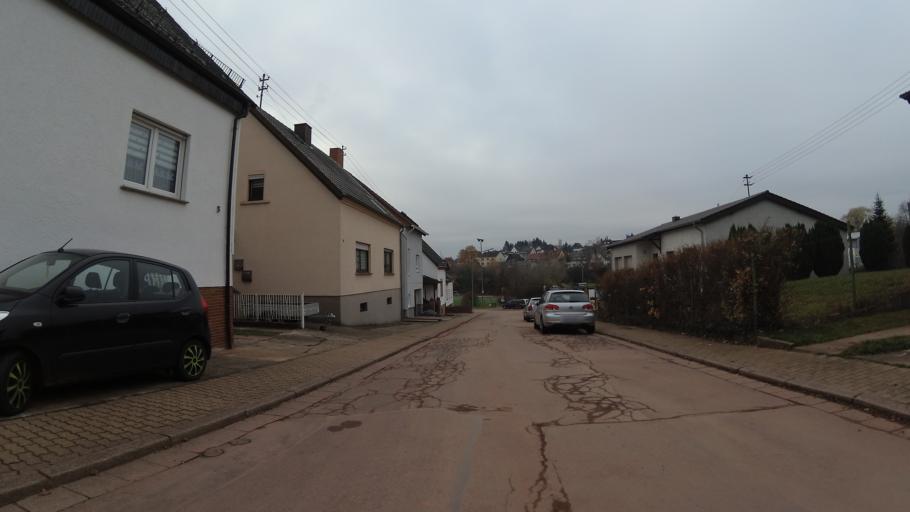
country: DE
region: Saarland
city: Illingen
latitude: 49.3733
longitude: 7.0502
